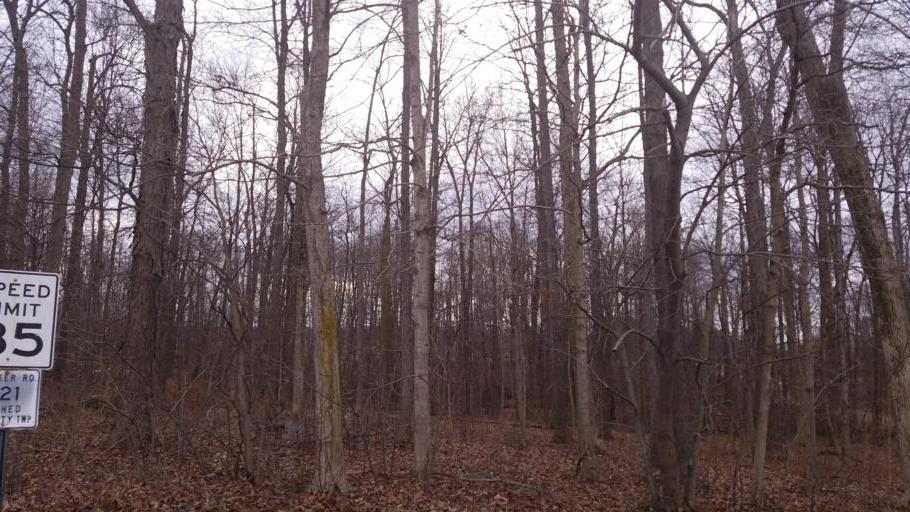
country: US
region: Ohio
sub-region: Knox County
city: Centerburg
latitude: 40.3435
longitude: -82.6079
